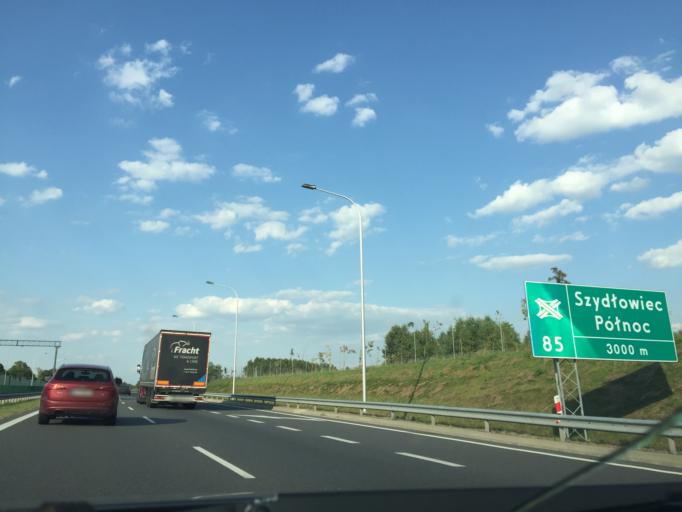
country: PL
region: Masovian Voivodeship
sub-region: Powiat szydlowiecki
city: Szydlowiec
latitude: 51.2406
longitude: 20.8779
